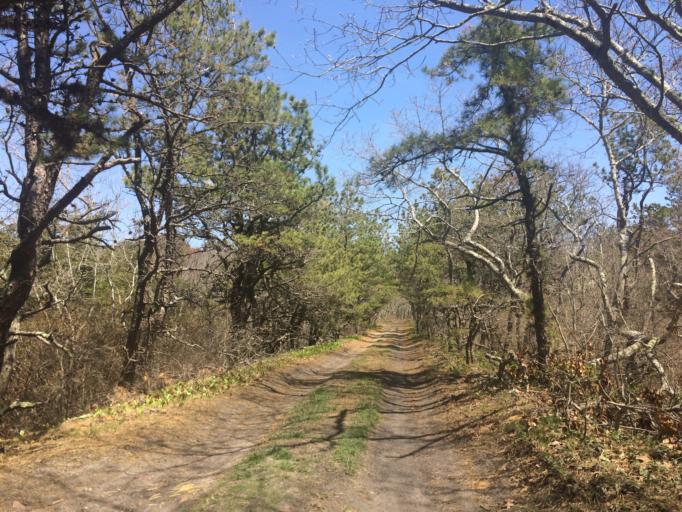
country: US
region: Massachusetts
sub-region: Barnstable County
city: Provincetown
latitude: 42.0643
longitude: -70.1678
